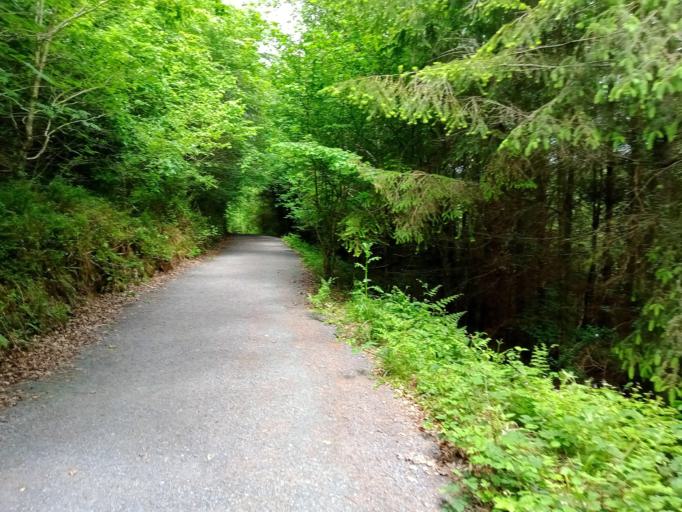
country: IE
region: Leinster
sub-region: Kilkenny
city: Thomastown
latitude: 52.4736
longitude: -7.0465
